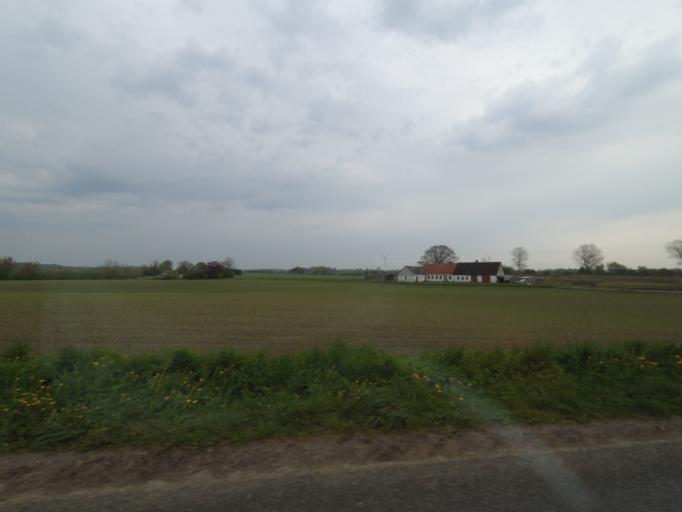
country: DK
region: South Denmark
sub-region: Svendborg Kommune
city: Svendborg
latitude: 55.1781
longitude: 10.5923
